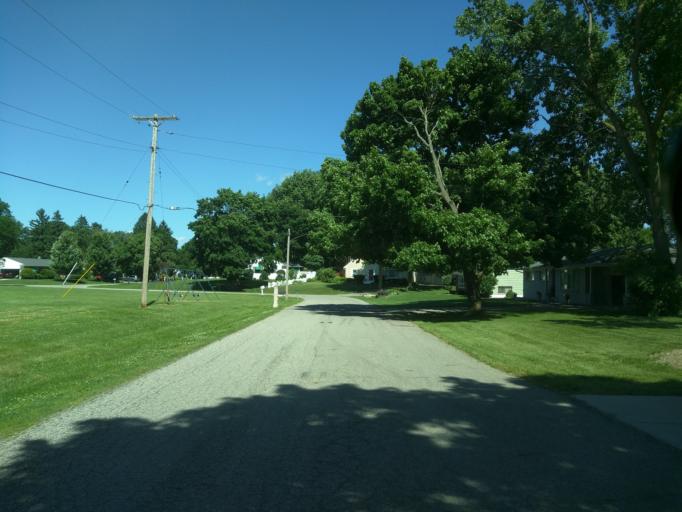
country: US
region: Michigan
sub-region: Ingham County
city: Edgemont Park
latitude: 42.7574
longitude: -84.6016
